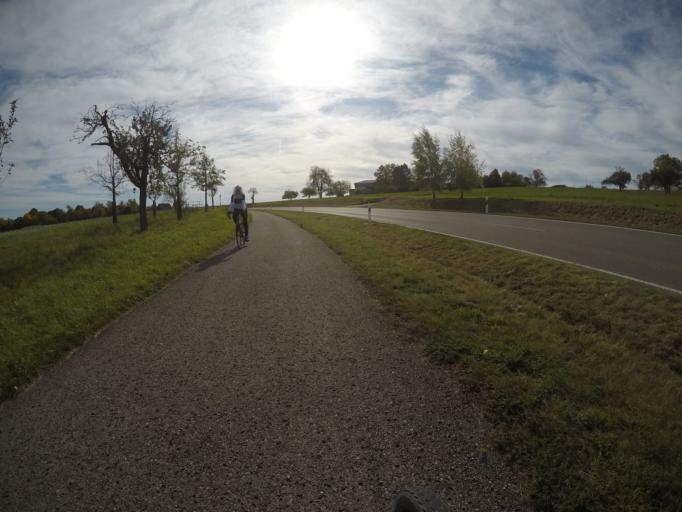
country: DE
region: Baden-Wuerttemberg
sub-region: Regierungsbezirk Stuttgart
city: Gartringen
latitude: 48.6473
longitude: 8.8890
